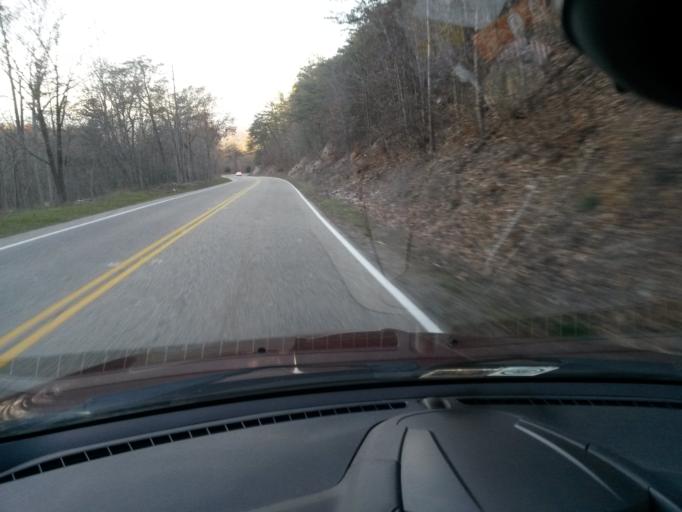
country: US
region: Virginia
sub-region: City of Buena Vista
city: Buena Vista
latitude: 37.7369
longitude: -79.3310
